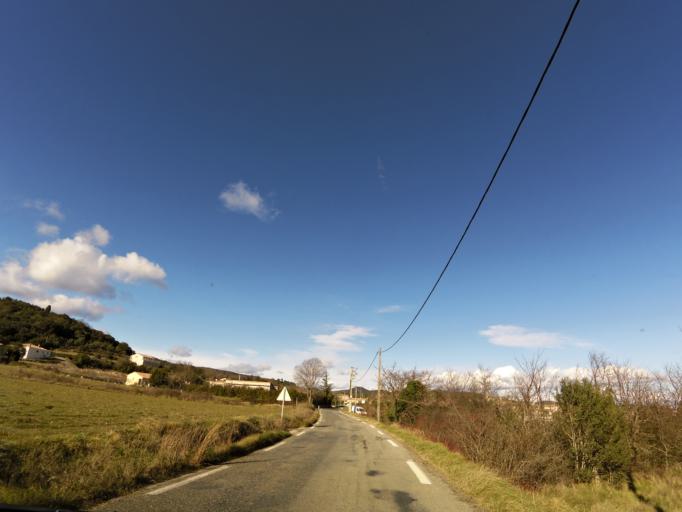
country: FR
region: Languedoc-Roussillon
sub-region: Departement du Gard
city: Sauve
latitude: 43.9853
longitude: 3.9517
